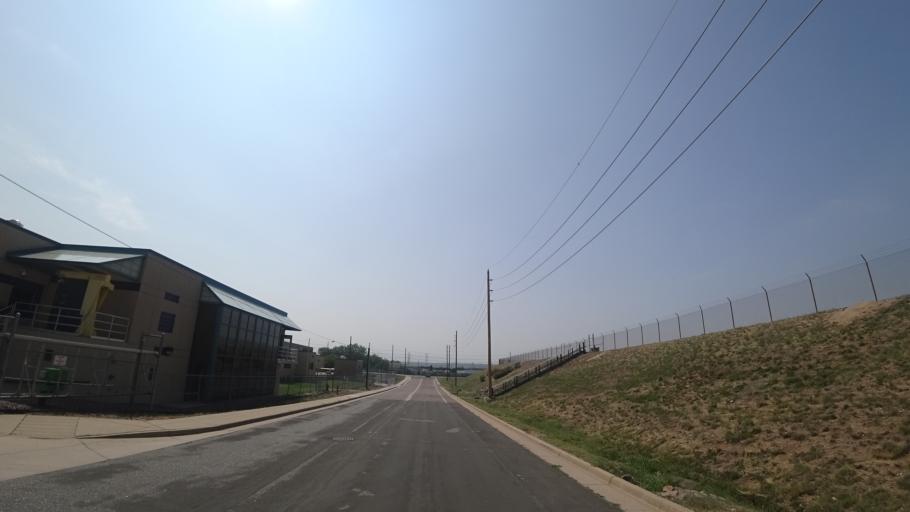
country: US
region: Colorado
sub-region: Arapahoe County
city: Littleton
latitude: 39.6295
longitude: -105.0045
